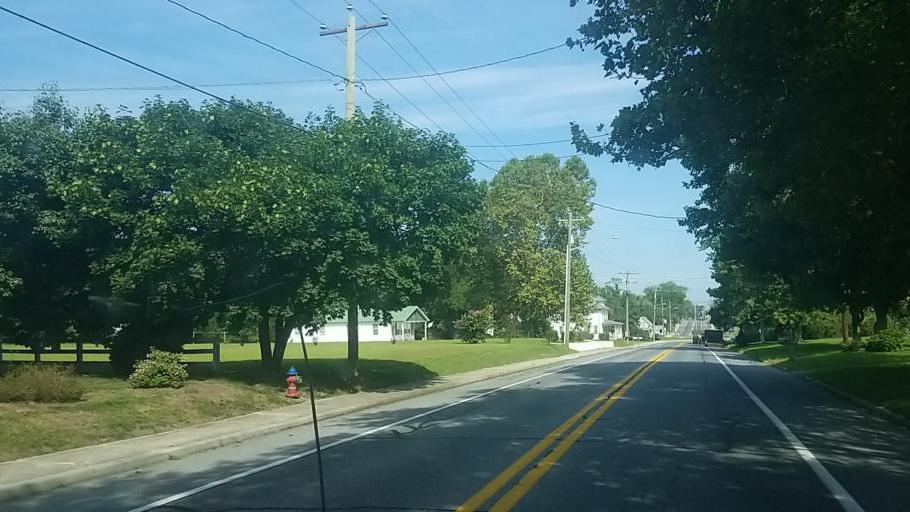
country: US
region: Delaware
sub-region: Sussex County
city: Millsboro
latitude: 38.5451
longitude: -75.2423
